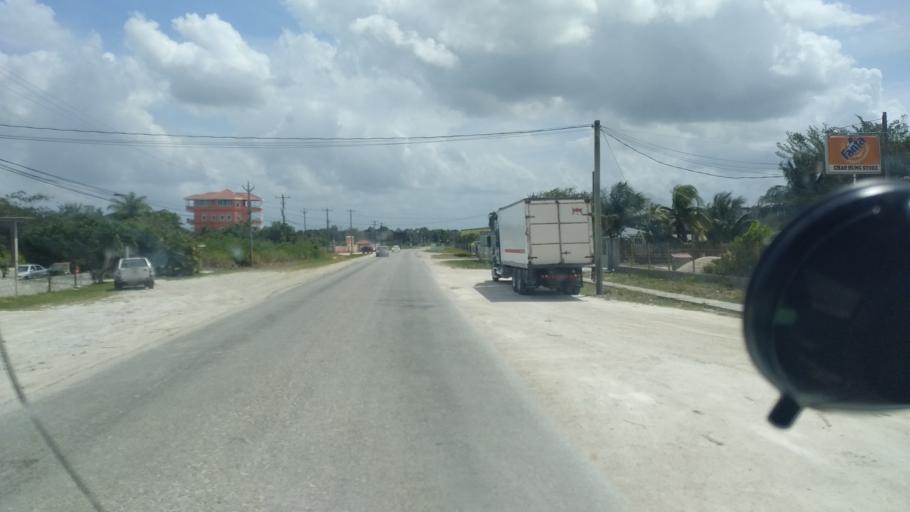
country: BZ
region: Orange Walk
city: Orange Walk
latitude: 18.0582
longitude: -88.5681
